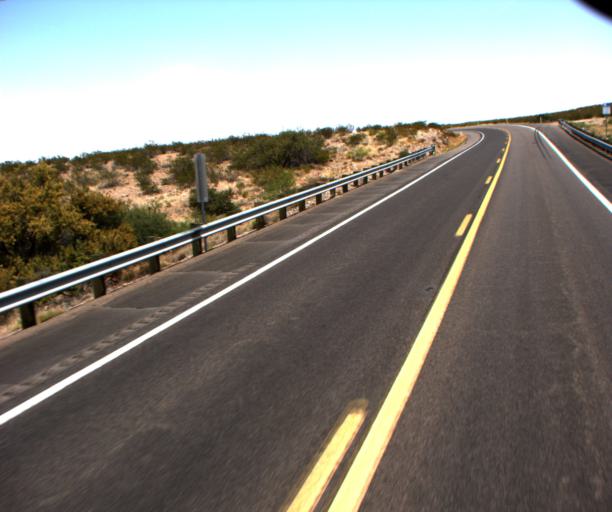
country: US
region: Arizona
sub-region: Greenlee County
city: Clifton
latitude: 32.7239
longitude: -109.1712
